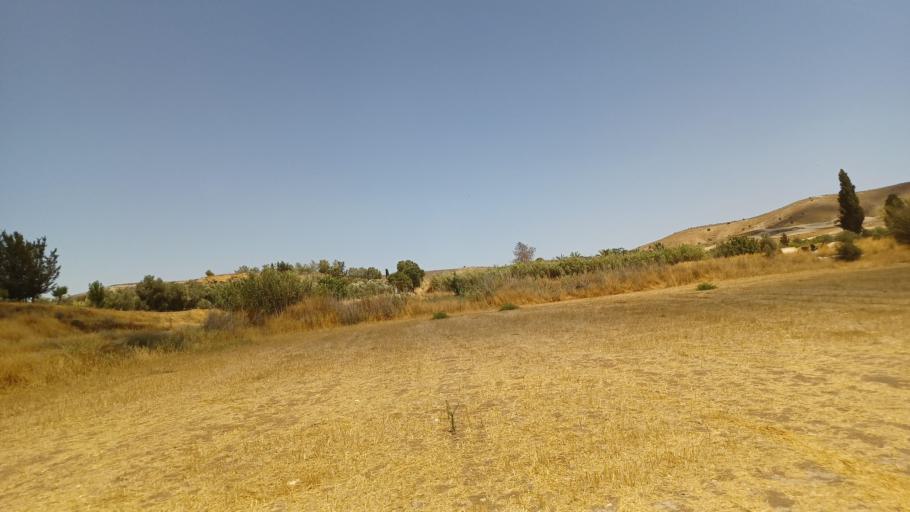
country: CY
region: Larnaka
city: Troulloi
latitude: 35.0387
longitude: 33.6170
